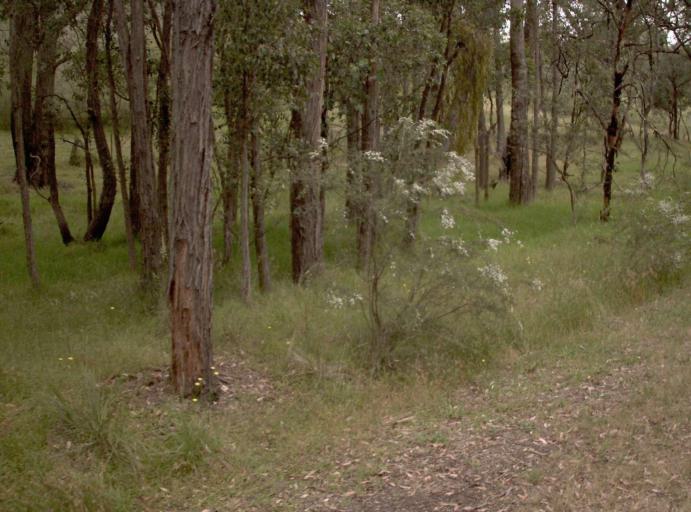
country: AU
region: Victoria
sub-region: East Gippsland
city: Bairnsdale
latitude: -37.7827
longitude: 147.3241
